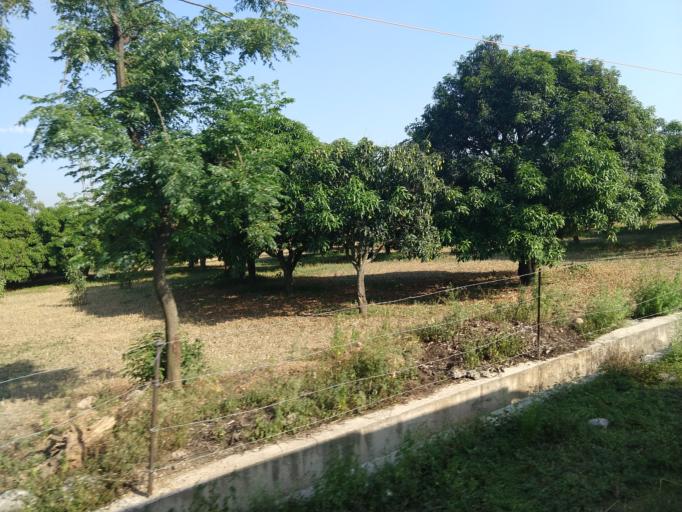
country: IN
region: Himachal Pradesh
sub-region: Chamba
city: Chowari
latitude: 32.3547
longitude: 75.9188
